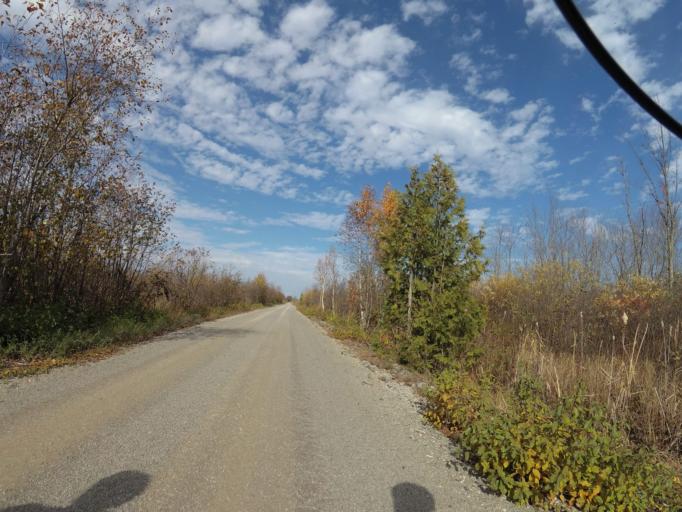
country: CA
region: Ontario
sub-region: Lanark County
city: Smiths Falls
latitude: 45.0224
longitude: -76.0760
